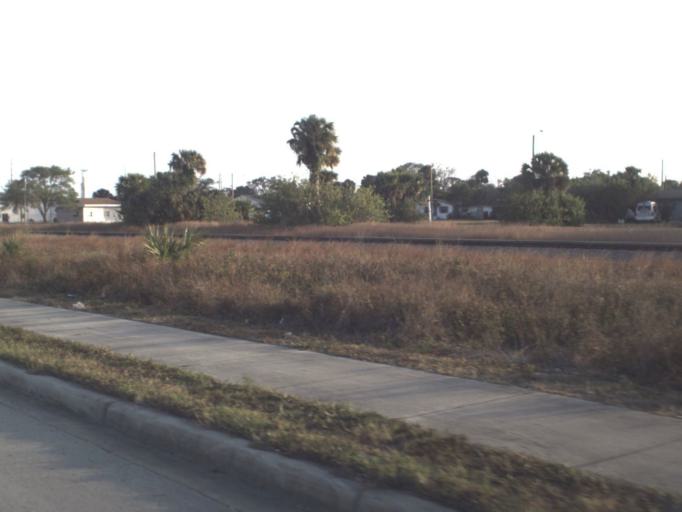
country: US
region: Florida
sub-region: Brevard County
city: Indian Harbour Beach
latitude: 28.1391
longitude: -80.6343
